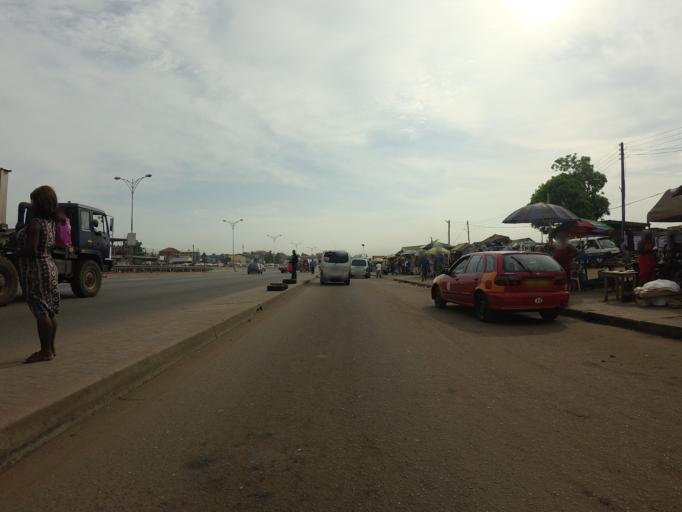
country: GH
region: Greater Accra
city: Dome
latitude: 5.6076
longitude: -0.2462
